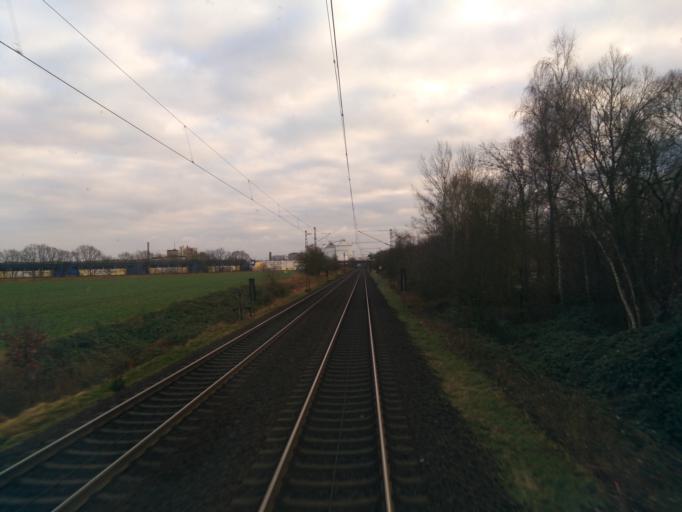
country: DE
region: Lower Saxony
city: Uelzen
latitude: 52.9916
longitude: 10.5490
